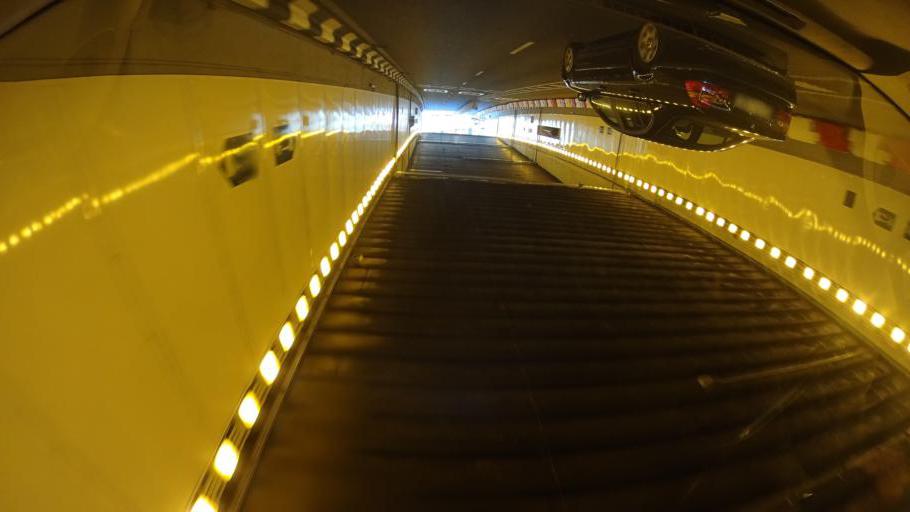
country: ES
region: Madrid
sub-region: Provincia de Madrid
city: Salamanca
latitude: 40.4452
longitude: -3.6855
